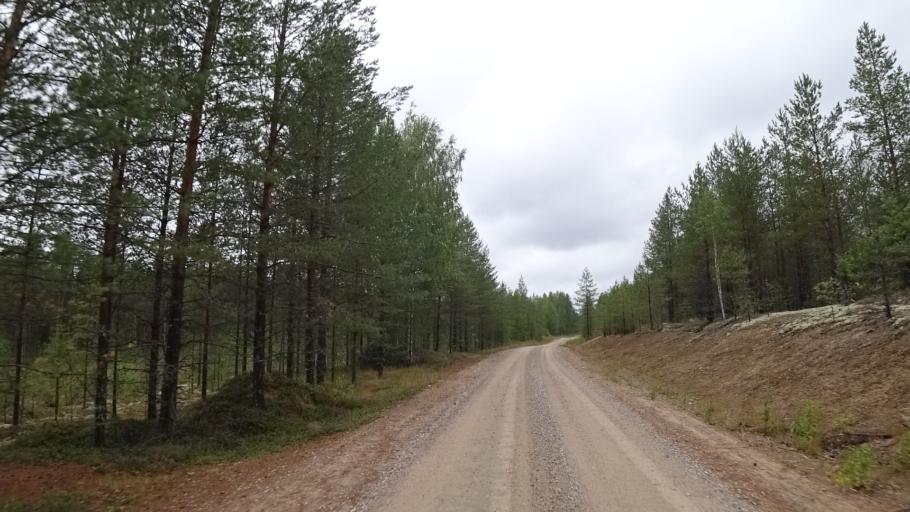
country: FI
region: North Karelia
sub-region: Pielisen Karjala
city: Lieksa
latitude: 63.5147
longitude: 30.1227
